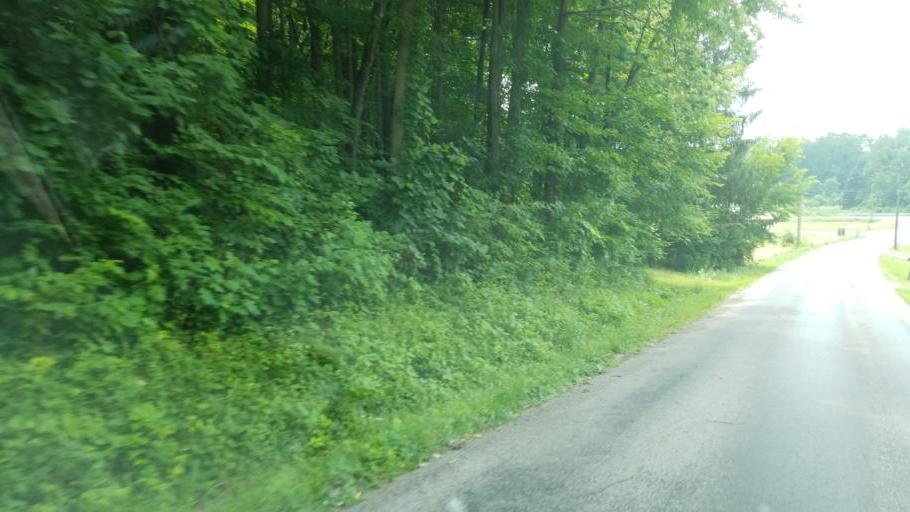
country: US
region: Ohio
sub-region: Licking County
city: Utica
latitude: 40.1639
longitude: -82.4253
